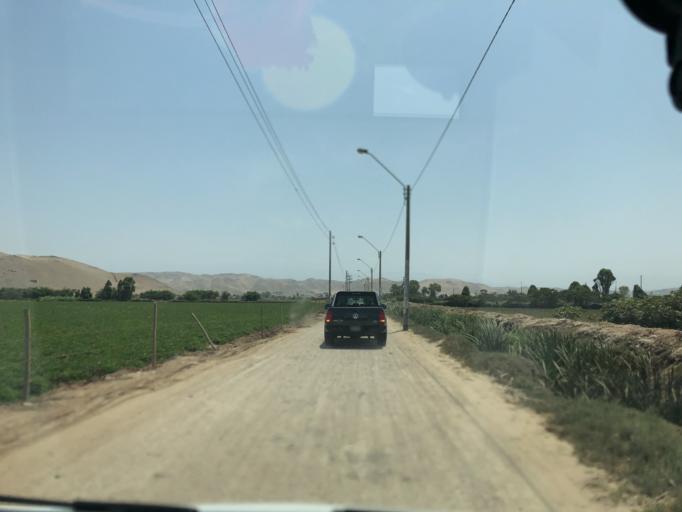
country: PE
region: Lima
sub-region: Provincia de Canete
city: San Vicente de Canete
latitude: -13.0228
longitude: -76.4700
